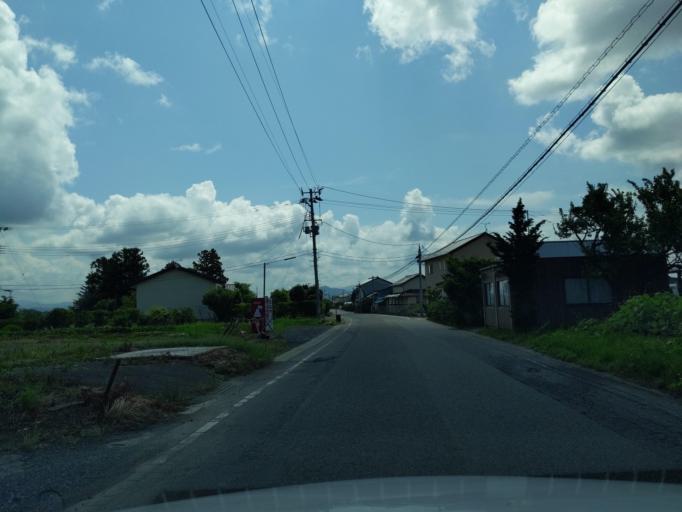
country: JP
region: Fukushima
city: Sukagawa
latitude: 37.3347
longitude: 140.3560
